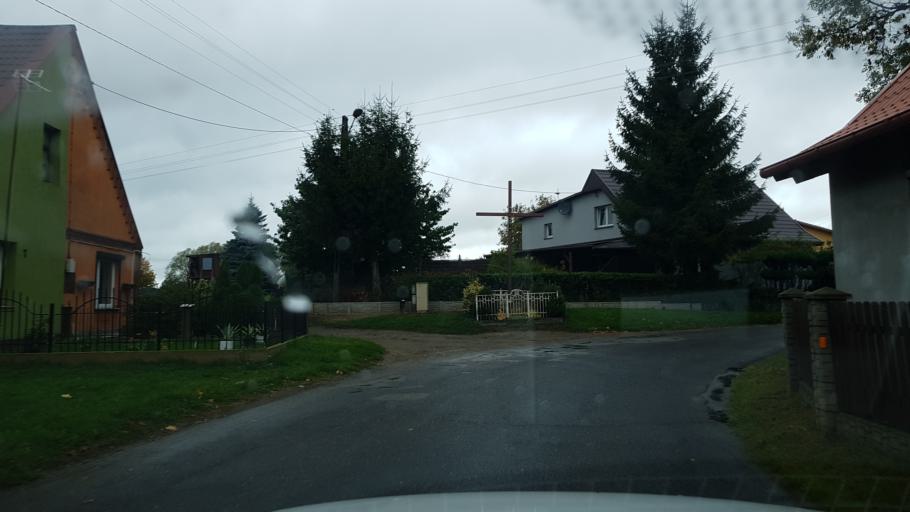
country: PL
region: West Pomeranian Voivodeship
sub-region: Powiat mysliborski
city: Mysliborz
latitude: 52.9734
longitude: 14.8844
